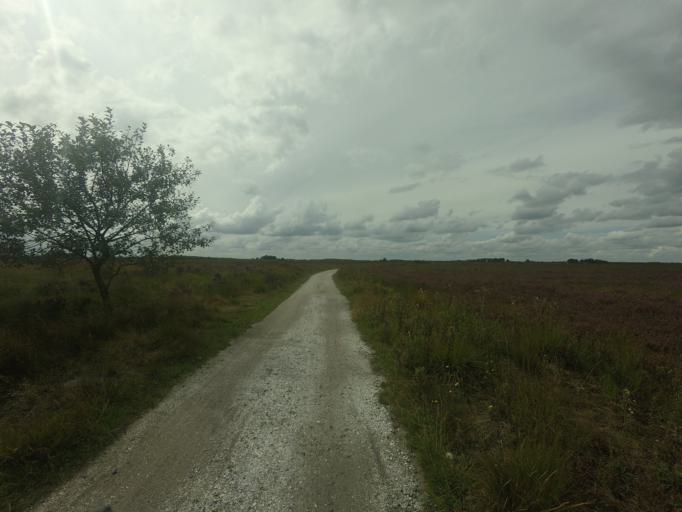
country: NL
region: Groningen
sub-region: Gemeente Leek
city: Leek
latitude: 53.0032
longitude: 6.3881
